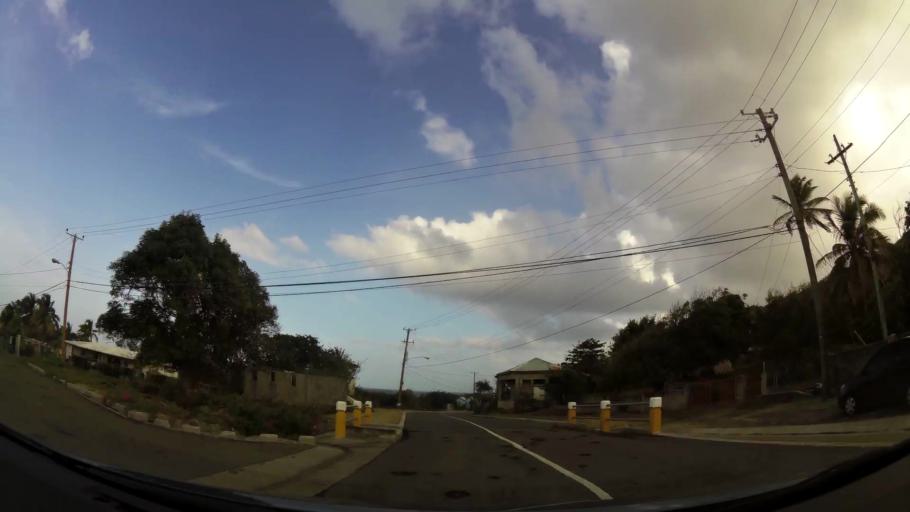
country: KN
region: Saint James Windwa
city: Newcastle
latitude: 17.1962
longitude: -62.5736
